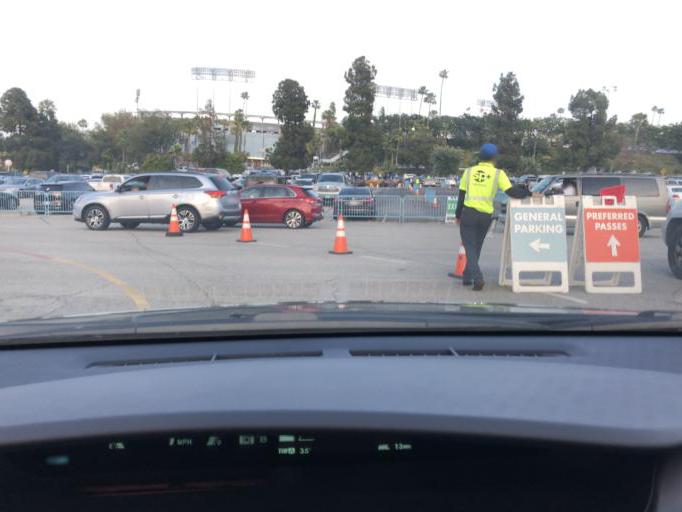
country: US
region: California
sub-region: Los Angeles County
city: Echo Park
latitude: 34.0746
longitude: -118.2437
